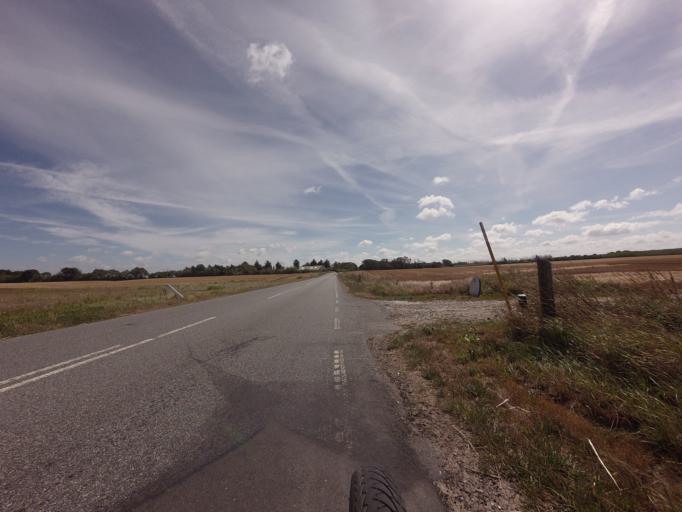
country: DK
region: North Denmark
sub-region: Hjorring Kommune
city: Vra
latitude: 57.3318
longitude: 9.8158
